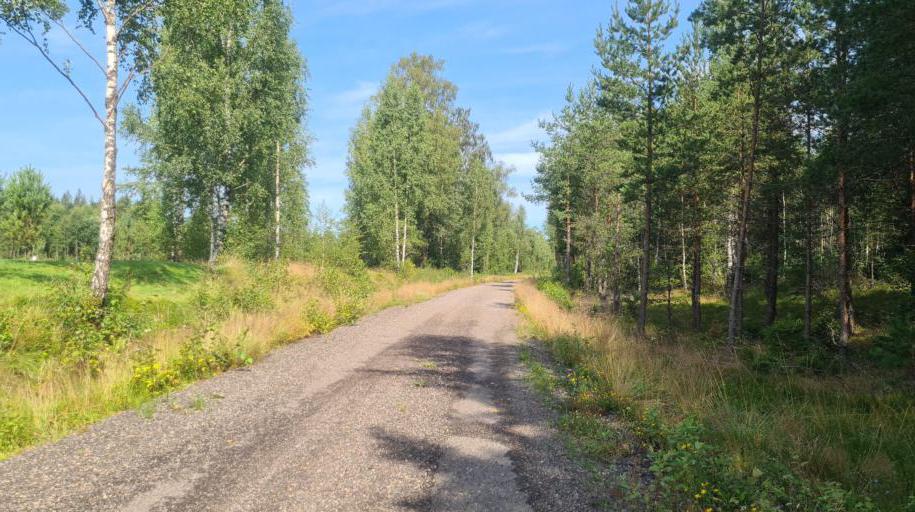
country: SE
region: Kronoberg
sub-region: Ljungby Kommun
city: Lagan
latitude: 56.9295
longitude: 13.9791
